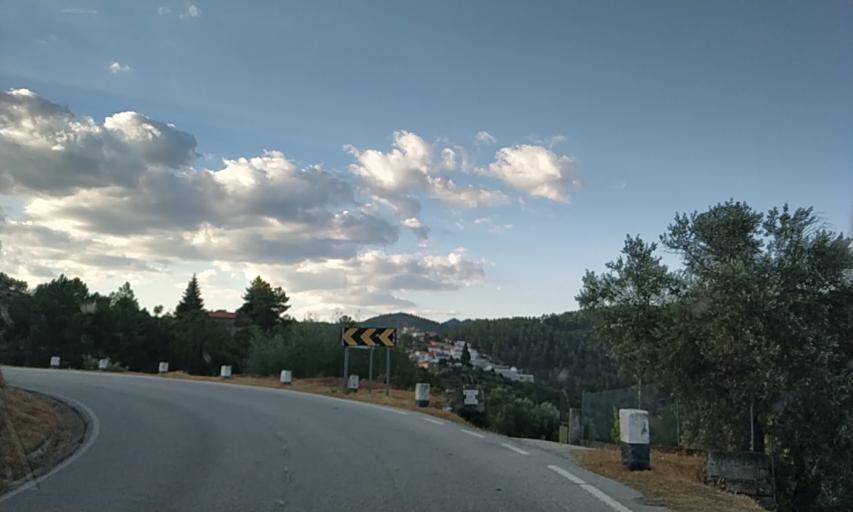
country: PT
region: Viseu
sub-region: Sao Joao da Pesqueira
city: Sao Joao da Pesqueira
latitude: 41.2435
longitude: -7.4308
